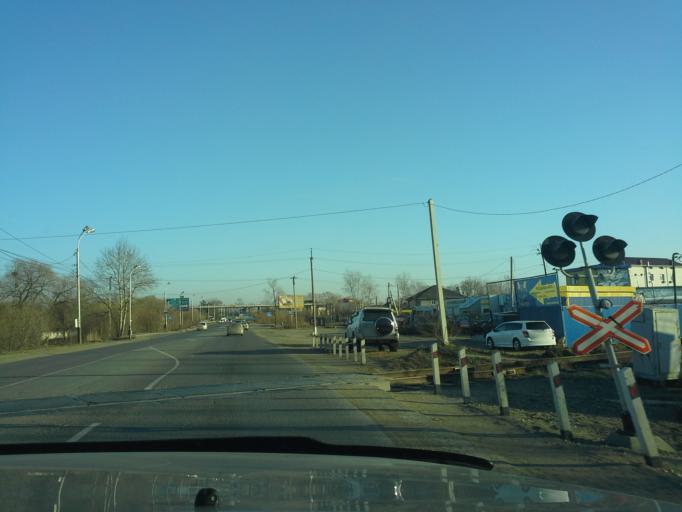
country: RU
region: Khabarovsk Krai
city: Topolevo
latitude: 48.4745
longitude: 135.1705
